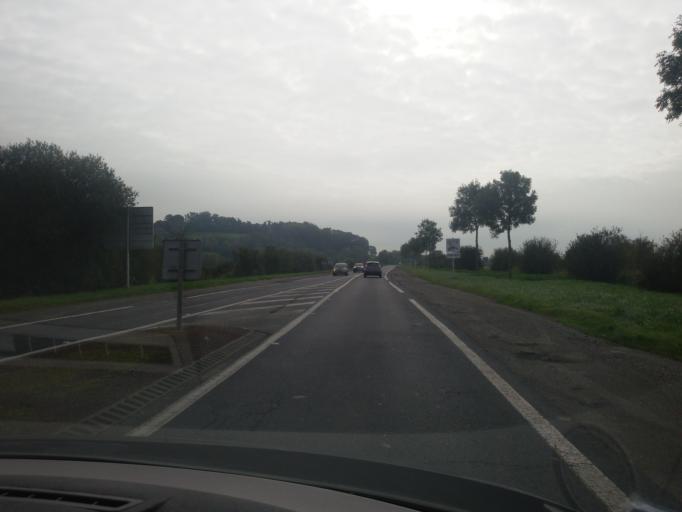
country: FR
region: Lower Normandy
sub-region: Departement du Calvados
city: Dives-sur-Mer
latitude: 49.2557
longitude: -0.1037
